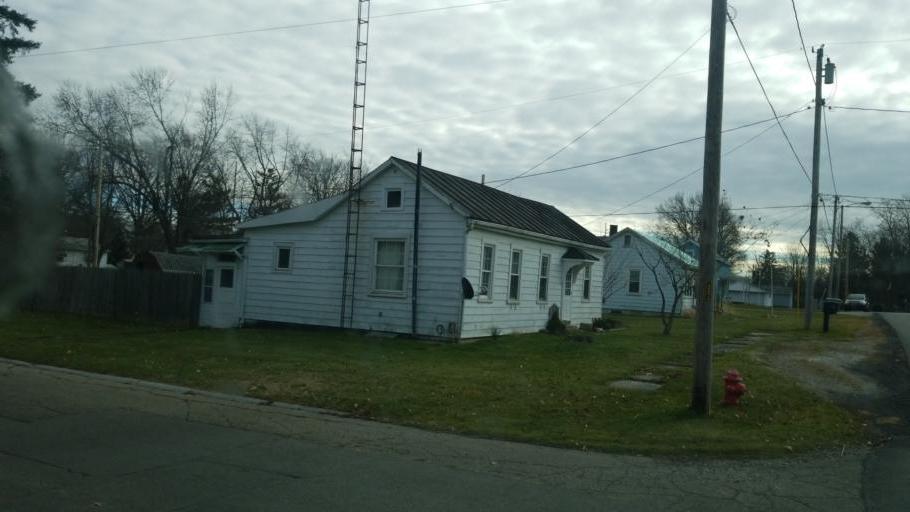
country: US
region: Ohio
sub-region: Crawford County
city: Galion
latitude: 40.7286
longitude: -82.8003
